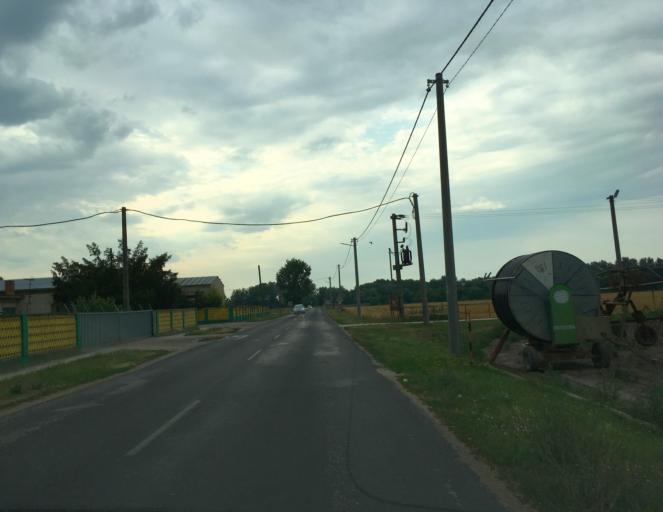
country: SK
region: Trnavsky
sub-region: Okres Dunajska Streda
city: Velky Meder
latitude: 47.8960
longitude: 17.7972
